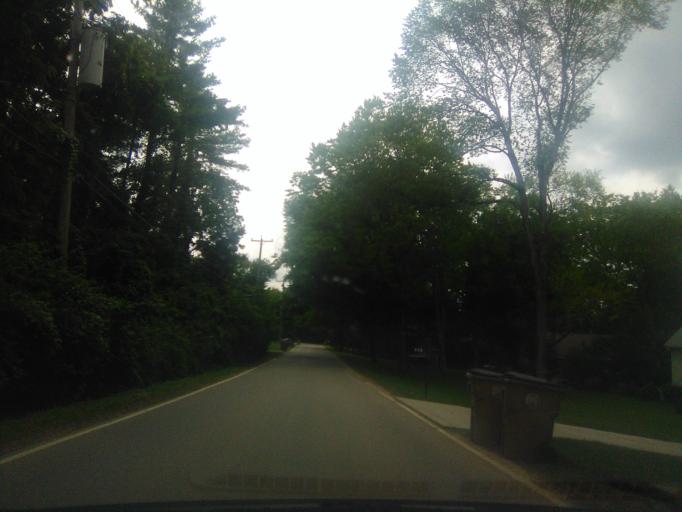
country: US
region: Tennessee
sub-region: Davidson County
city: Belle Meade
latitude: 36.0913
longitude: -86.8760
